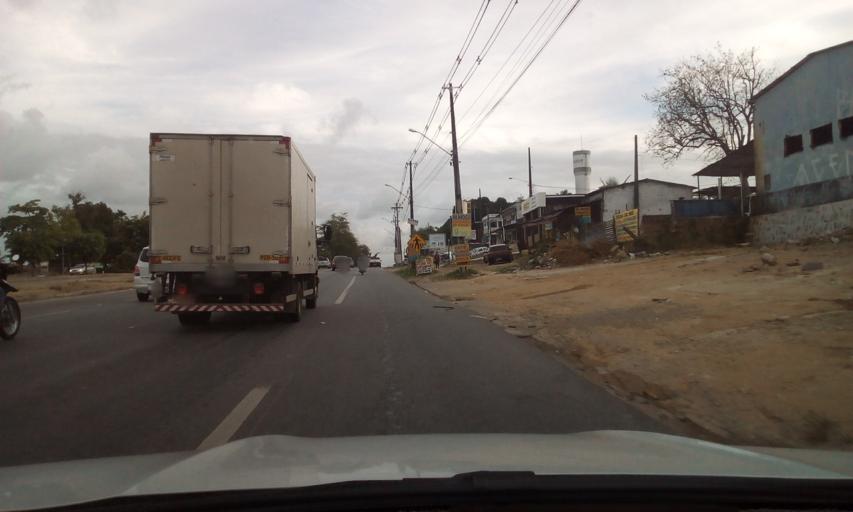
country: BR
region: Pernambuco
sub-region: Igarassu
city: Igarassu
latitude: -7.8584
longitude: -34.9084
